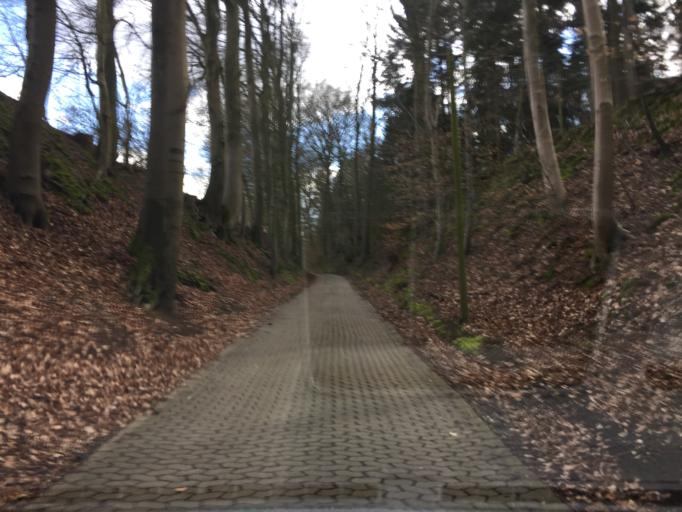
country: DE
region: Lower Saxony
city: Bruchhausen-Vilsen
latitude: 52.8026
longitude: 8.9962
